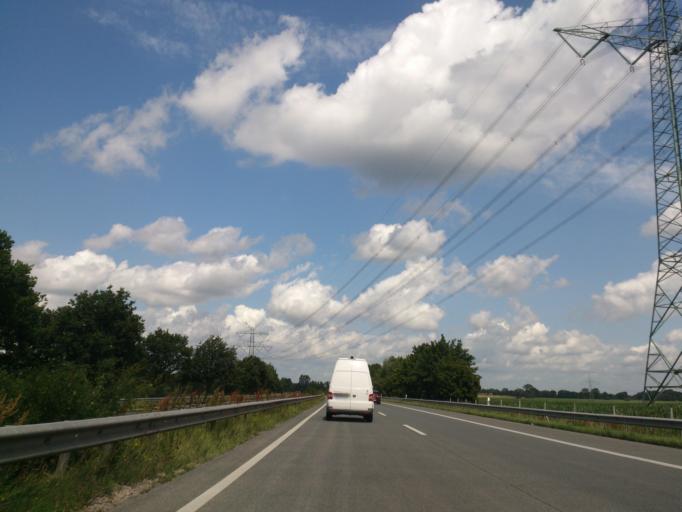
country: DE
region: Schleswig-Holstein
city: Klein Offenseth-Sparrieshoop
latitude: 53.7828
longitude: 9.7041
